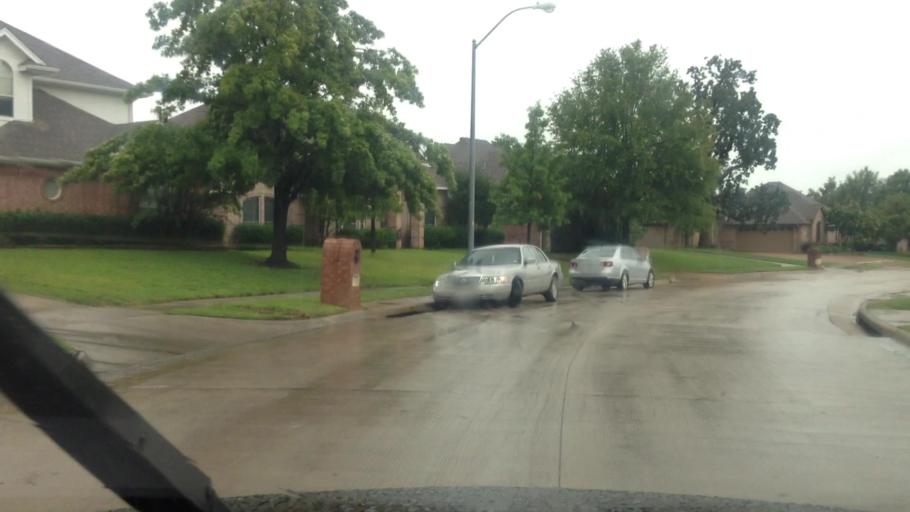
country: US
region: Texas
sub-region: Tarrant County
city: Colleyville
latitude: 32.9009
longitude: -97.2040
